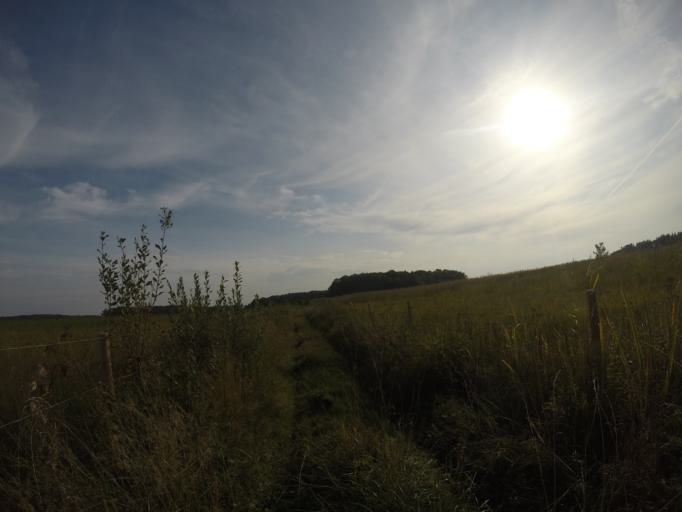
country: SE
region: Vaestmanland
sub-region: Hallstahammars Kommun
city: Kolback
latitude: 59.4767
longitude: 16.2175
